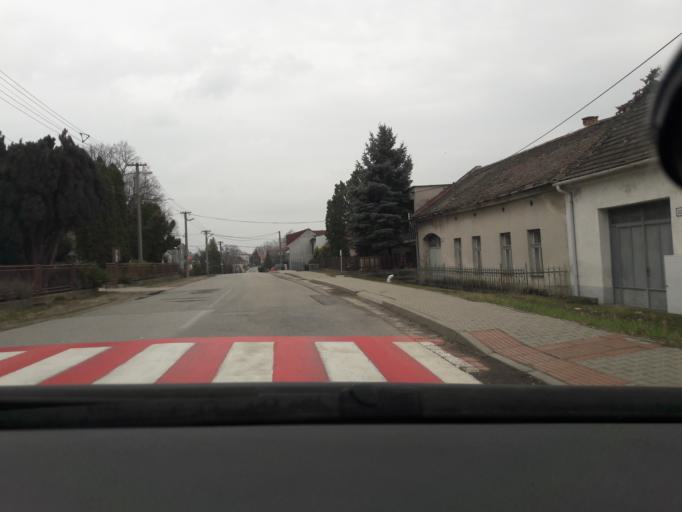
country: SK
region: Bratislavsky
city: Senec
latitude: 48.3083
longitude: 17.4448
